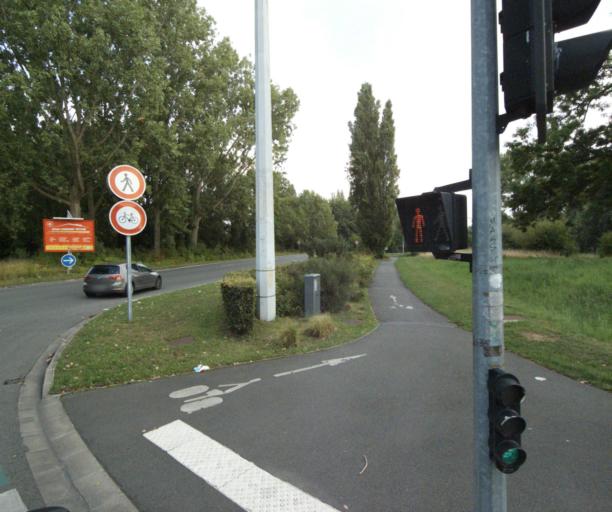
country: FR
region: Nord-Pas-de-Calais
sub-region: Departement du Nord
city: La Madeleine
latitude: 50.6476
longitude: 3.0687
